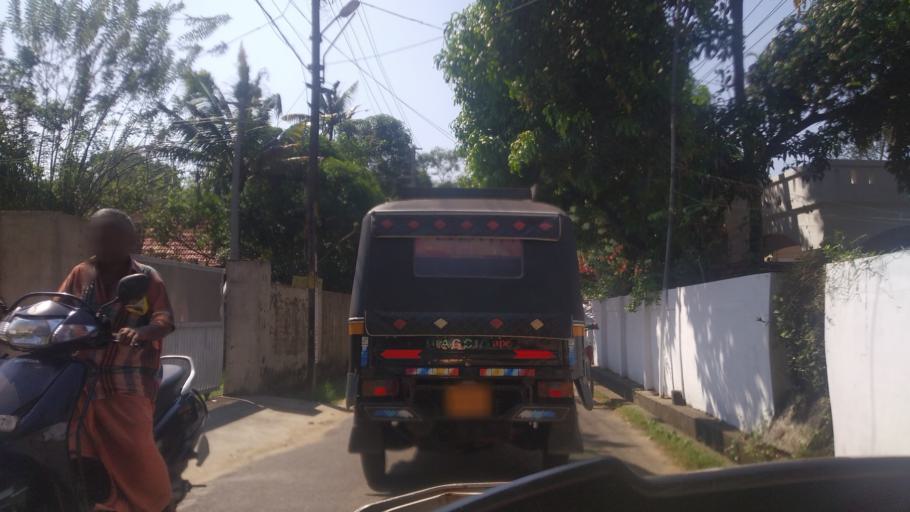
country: IN
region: Kerala
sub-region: Ernakulam
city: Elur
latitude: 10.0359
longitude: 76.2251
